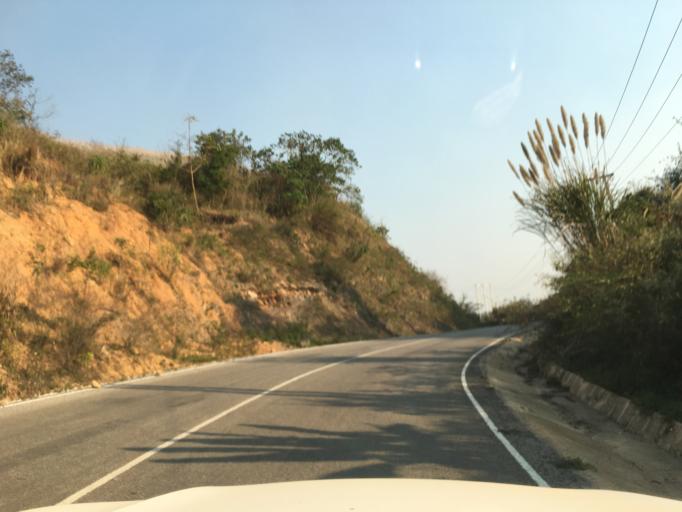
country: LA
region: Houaphan
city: Xam Nua
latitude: 20.5683
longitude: 104.0571
